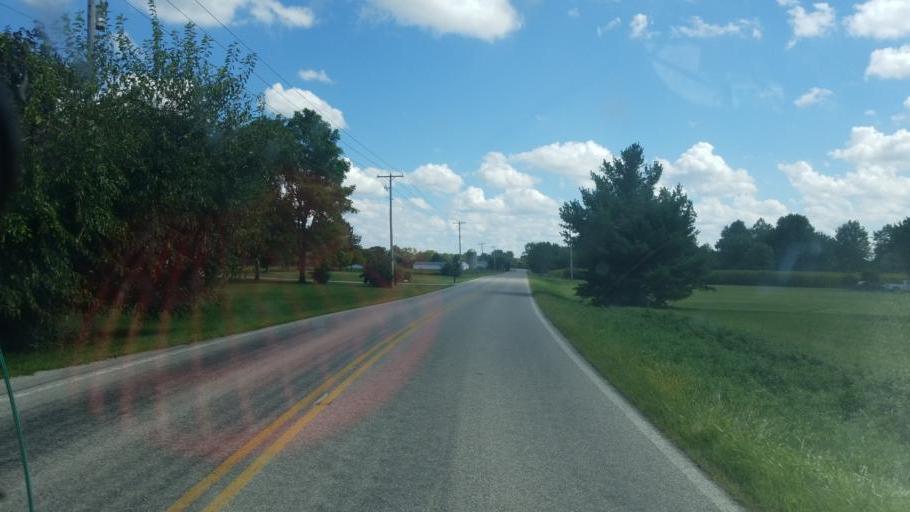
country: US
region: Ohio
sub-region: Marion County
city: Prospect
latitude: 40.3292
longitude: -83.1978
